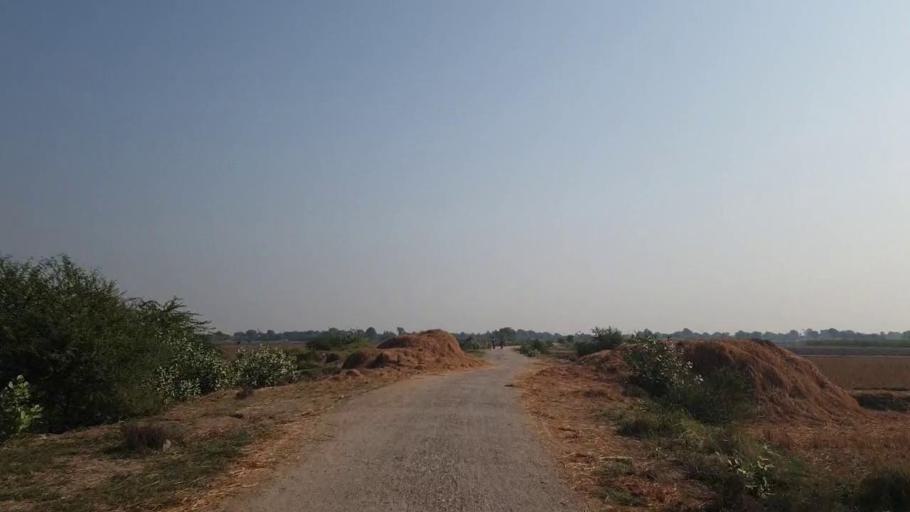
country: PK
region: Sindh
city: Matli
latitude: 25.0047
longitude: 68.6254
